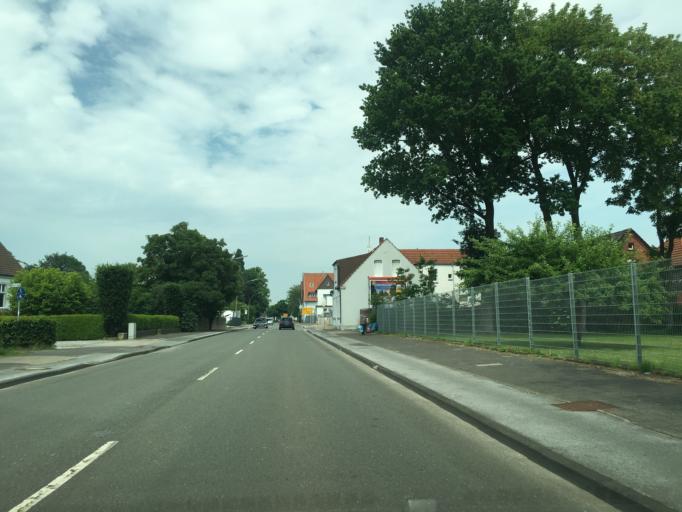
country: DE
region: North Rhine-Westphalia
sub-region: Regierungsbezirk Munster
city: Steinfurt
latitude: 52.1161
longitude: 7.3976
